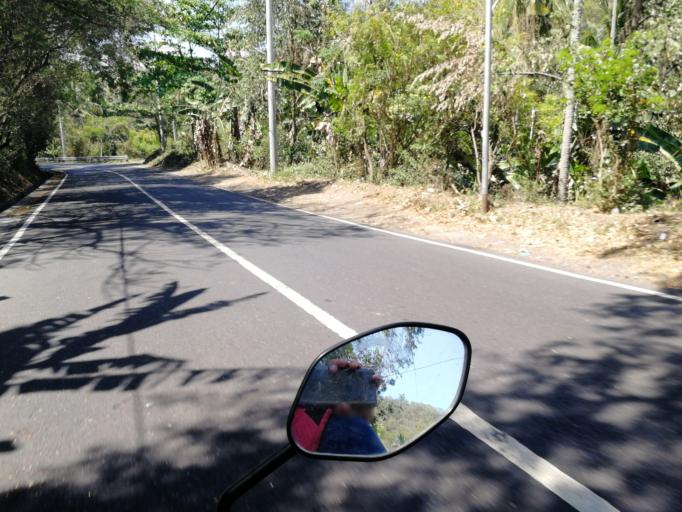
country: ID
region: Bali
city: Padangbai
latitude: -8.5262
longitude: 115.5042
